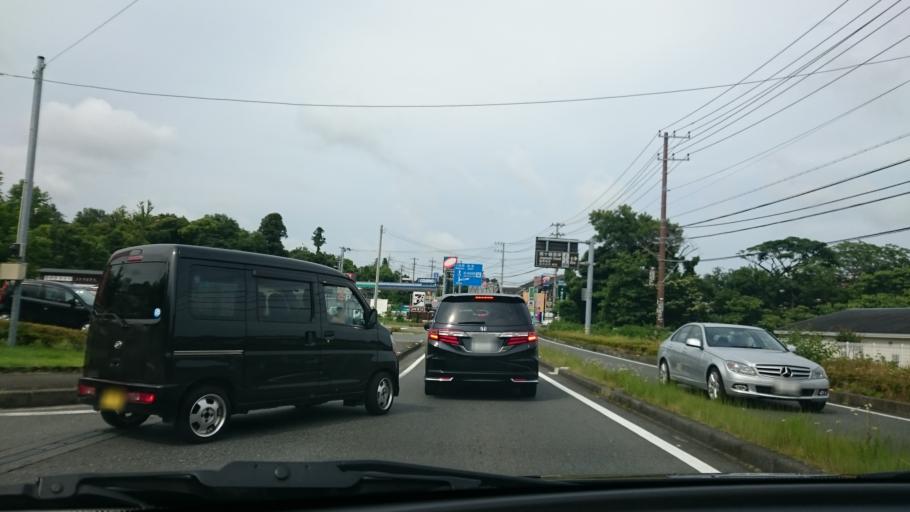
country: JP
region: Shizuoka
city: Ito
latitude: 34.8815
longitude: 139.1078
